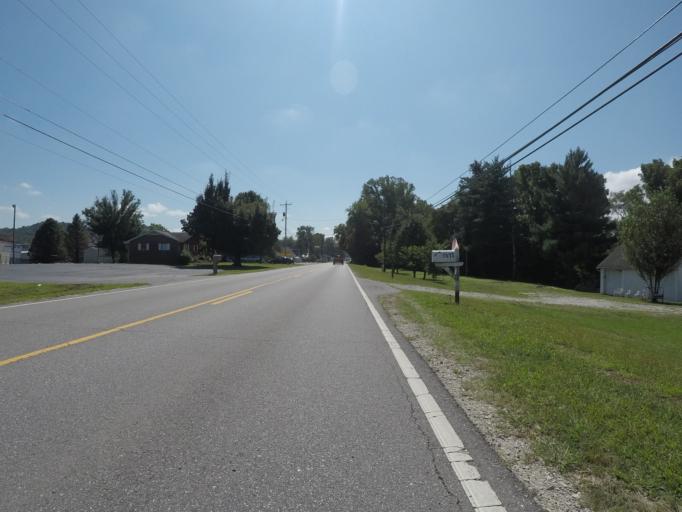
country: US
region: Ohio
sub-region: Lawrence County
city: South Point
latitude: 38.4543
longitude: -82.5955
